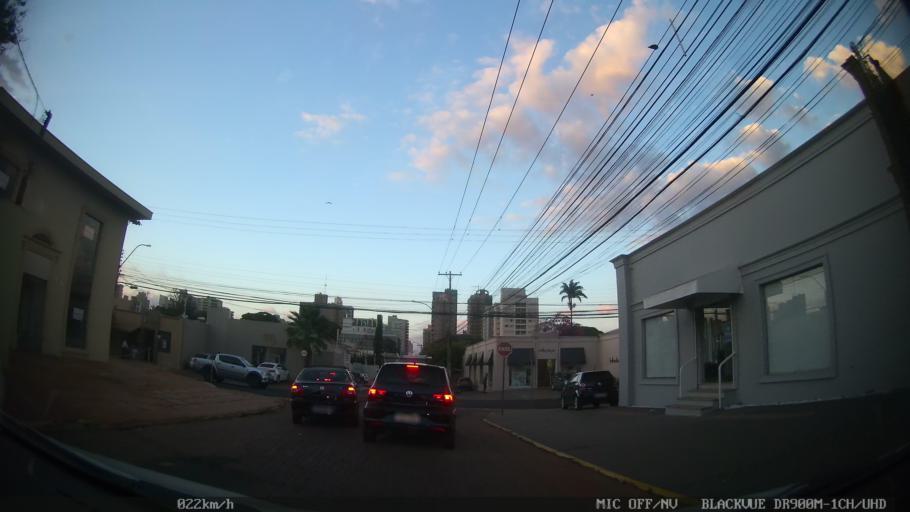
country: BR
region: Sao Paulo
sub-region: Ribeirao Preto
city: Ribeirao Preto
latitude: -21.1879
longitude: -47.8095
